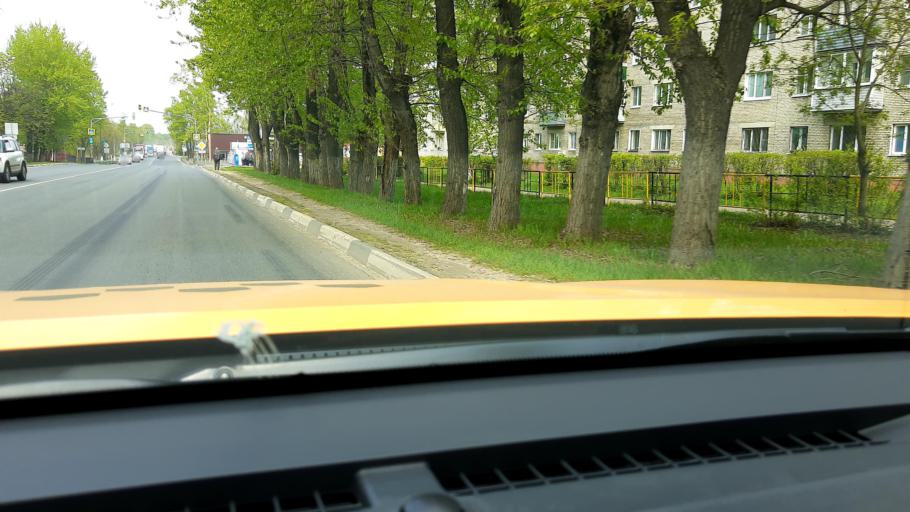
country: RU
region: Moskovskaya
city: Noginsk
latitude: 55.8780
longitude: 38.4305
